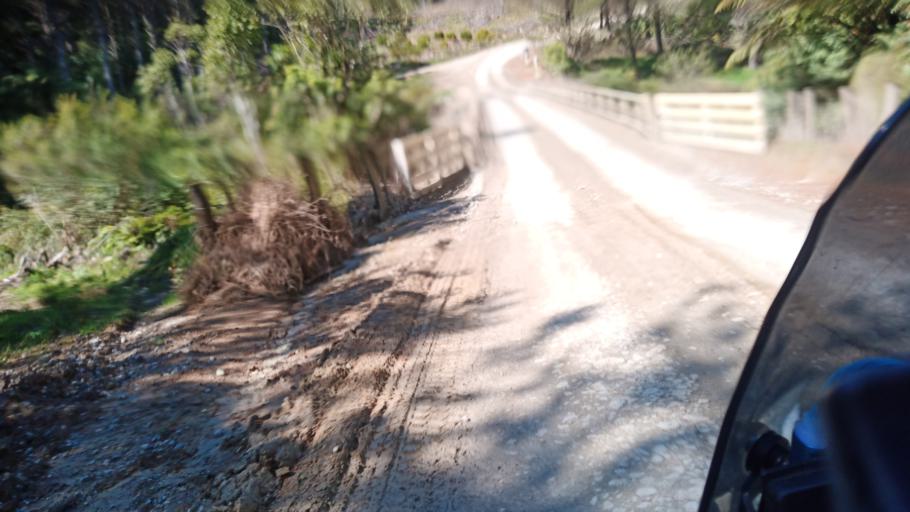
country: NZ
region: Gisborne
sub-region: Gisborne District
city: Gisborne
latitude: -38.8947
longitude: 177.8007
